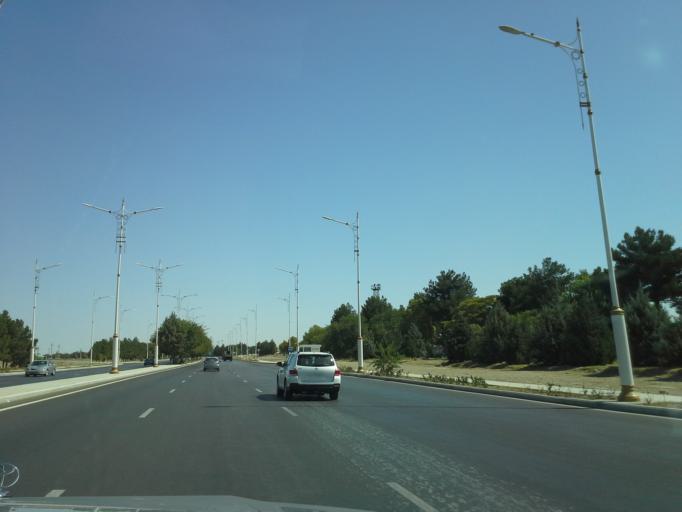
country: TM
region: Ahal
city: Ashgabat
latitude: 37.9226
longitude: 58.4411
